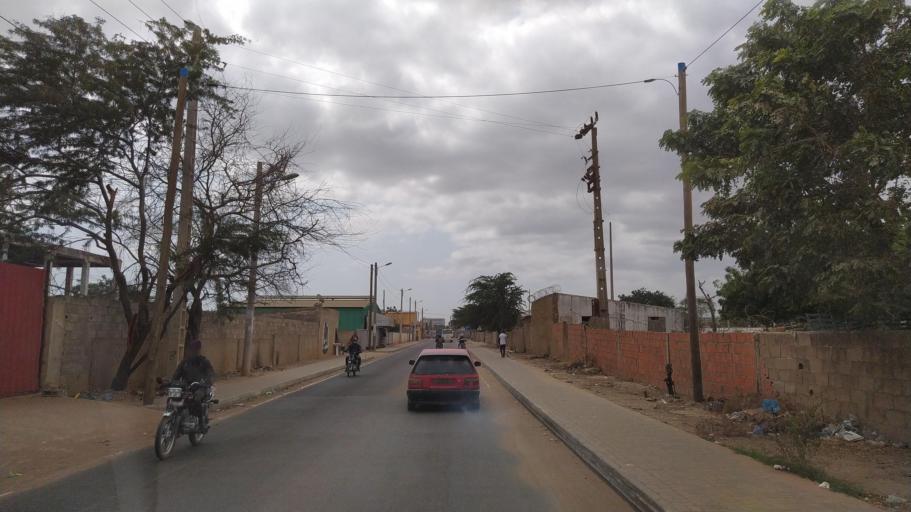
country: AO
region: Luanda
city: Luanda
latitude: -8.9723
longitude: 13.1501
